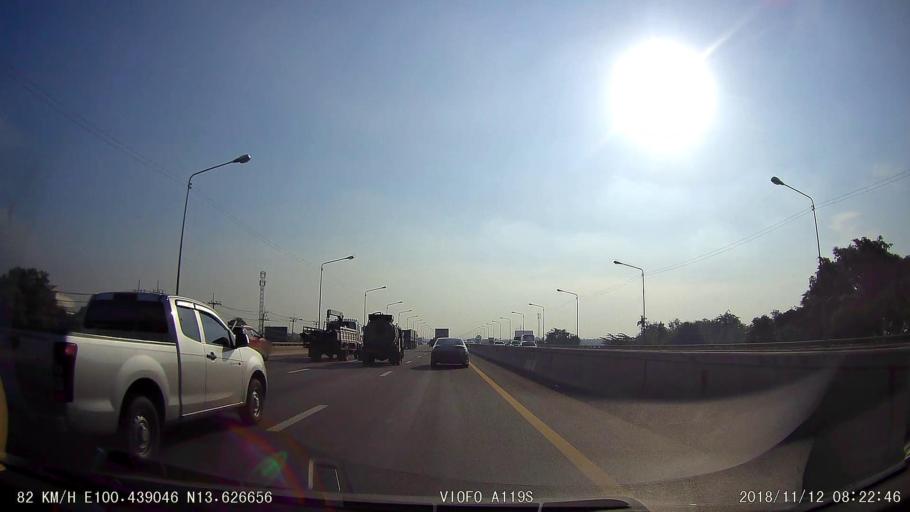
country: TH
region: Bangkok
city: Bang Khun Thian
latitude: 13.6269
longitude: 100.4393
